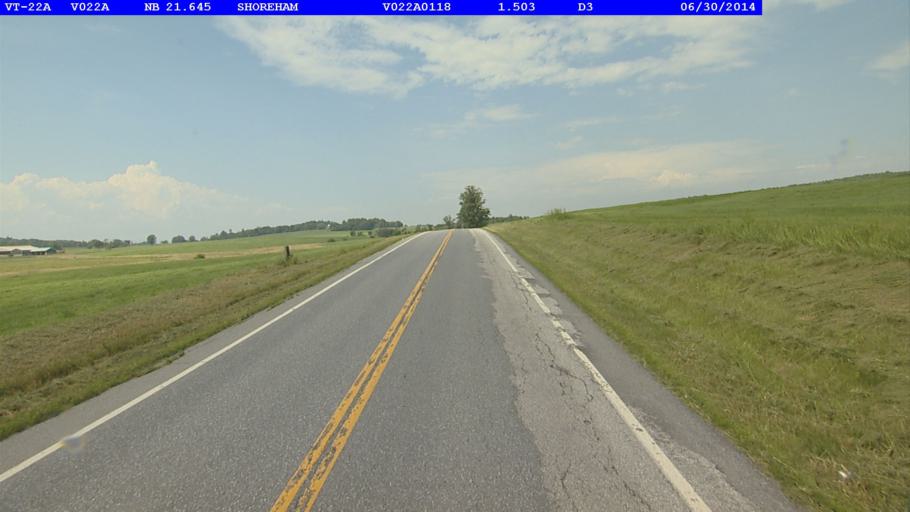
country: US
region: New York
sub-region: Essex County
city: Ticonderoga
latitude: 43.8712
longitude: -73.3096
